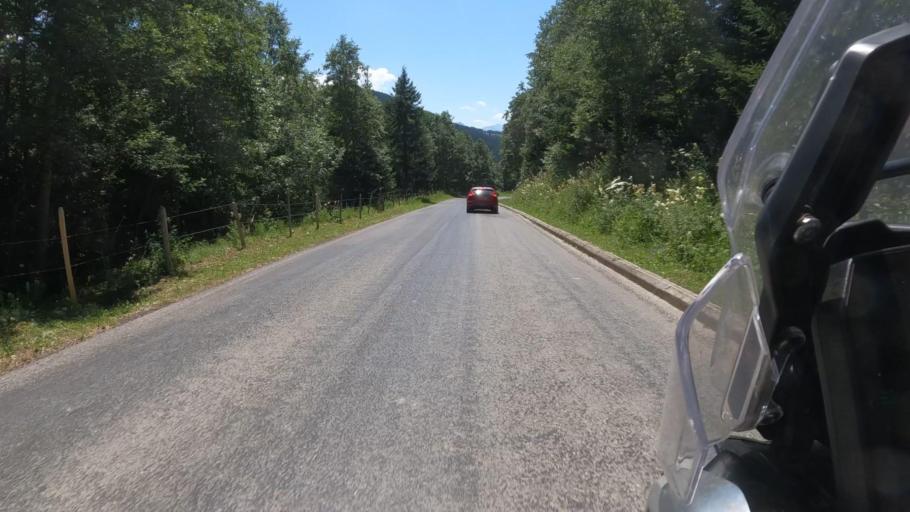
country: CH
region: Vaud
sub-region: Aigle District
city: Villars-sur-Ollon
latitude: 46.3130
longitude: 7.1060
